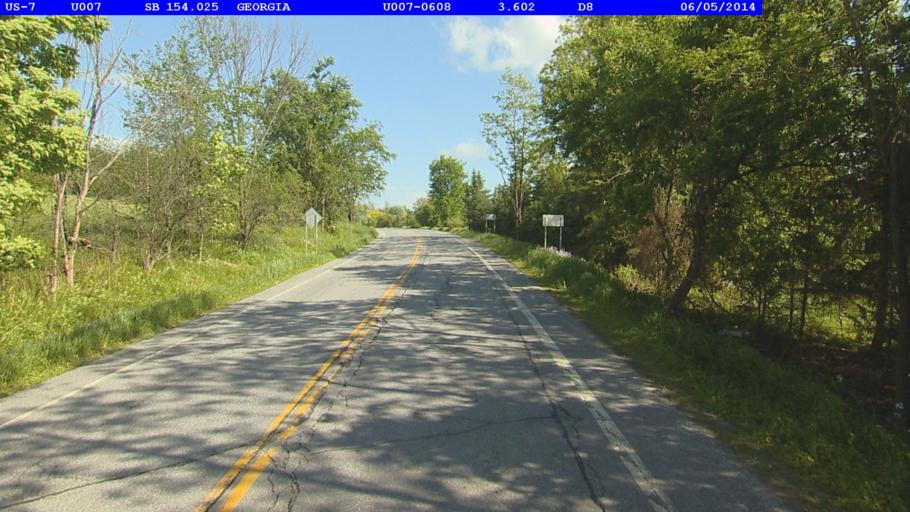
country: US
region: Vermont
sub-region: Chittenden County
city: Milton
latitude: 44.7233
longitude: -73.1182
